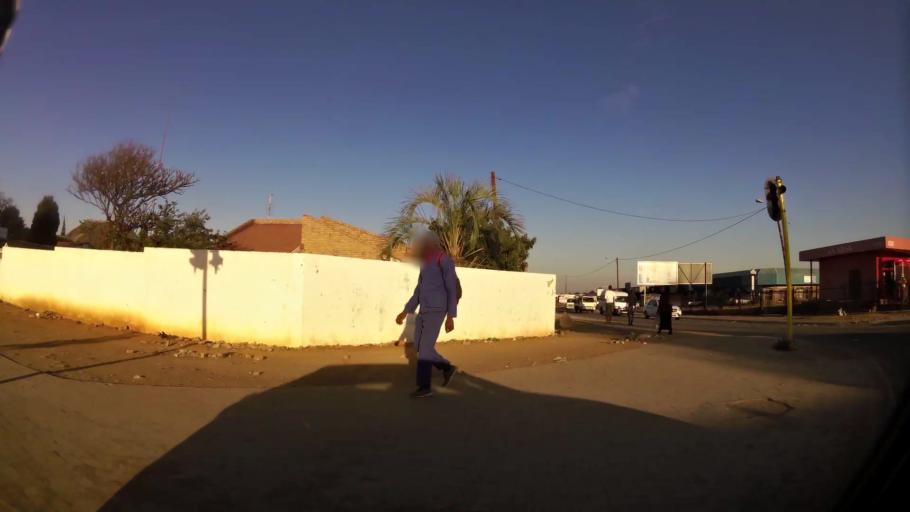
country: ZA
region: North-West
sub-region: Bojanala Platinum District Municipality
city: Rustenburg
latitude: -25.6373
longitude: 27.2115
